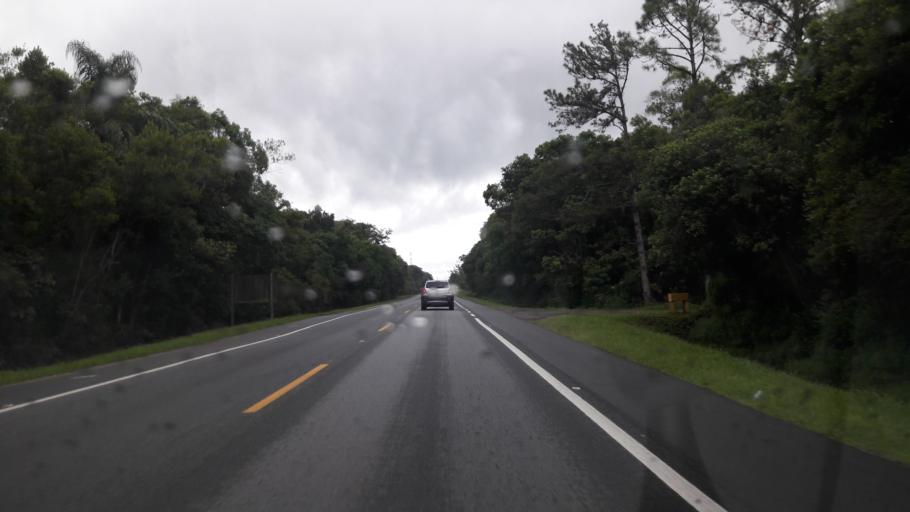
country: BR
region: Parana
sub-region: Pontal Do Parana
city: Pontal do Parana
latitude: -25.6502
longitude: -48.5266
